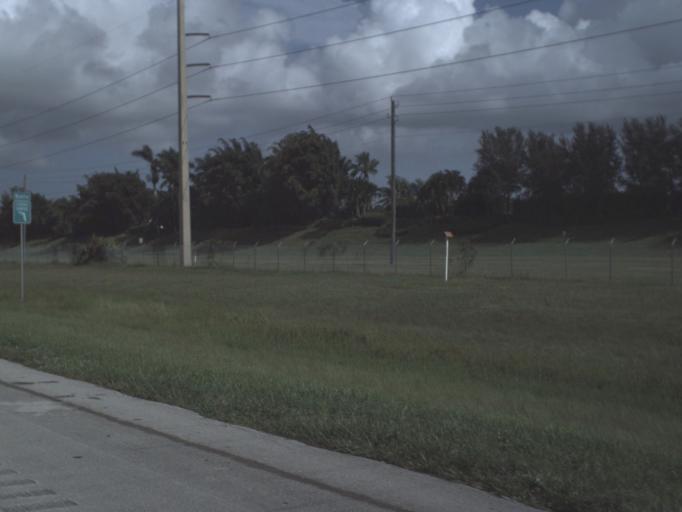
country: US
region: Florida
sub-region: Martin County
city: North River Shores
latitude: 27.2197
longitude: -80.3384
